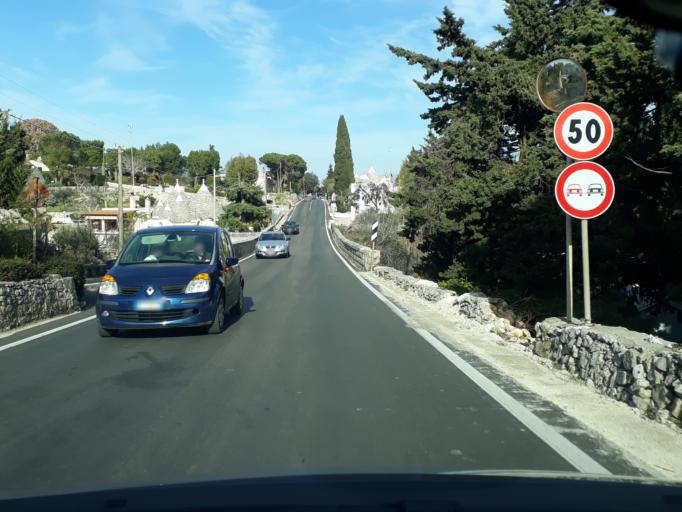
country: IT
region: Apulia
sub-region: Provincia di Brindisi
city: Lamie di Olimpie-Selva
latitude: 40.7939
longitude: 17.3480
